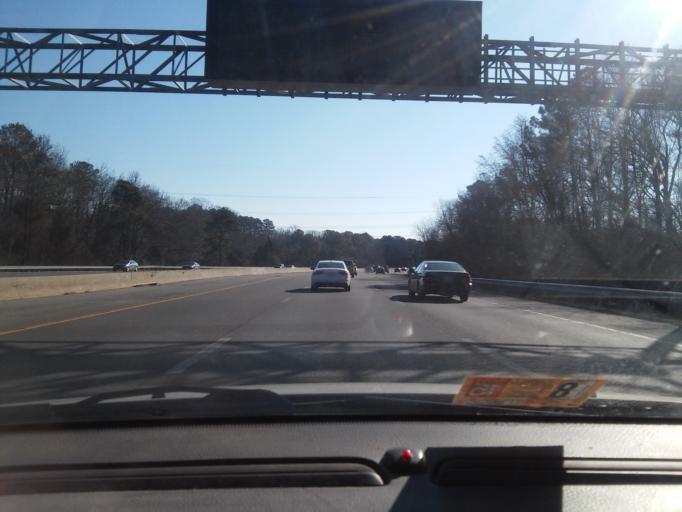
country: US
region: Virginia
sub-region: Henrico County
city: Tuckahoe
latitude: 37.6204
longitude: -77.5463
